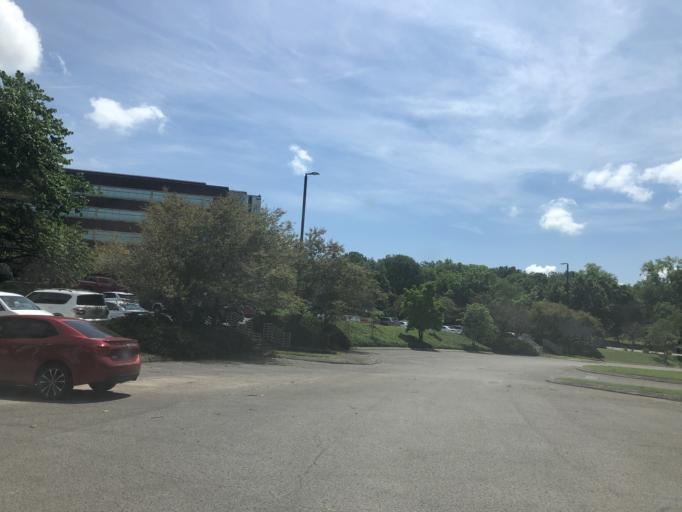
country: US
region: Tennessee
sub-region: Davidson County
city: Lakewood
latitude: 36.2536
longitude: -86.6832
